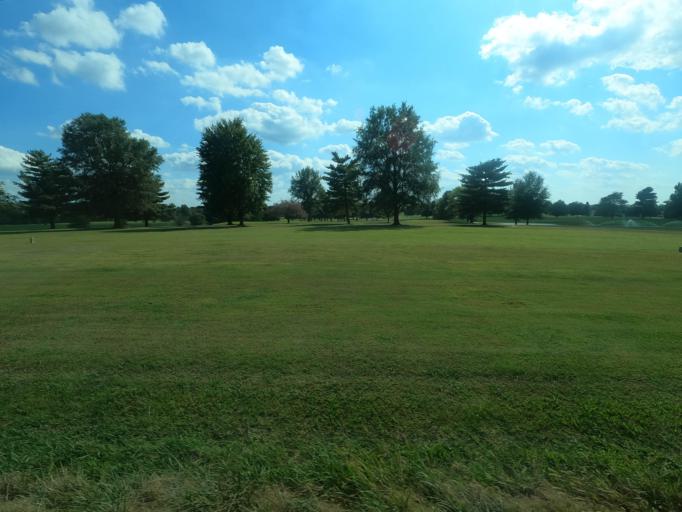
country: US
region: Illinois
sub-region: Massac County
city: Metropolis
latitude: 37.1912
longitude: -88.6966
